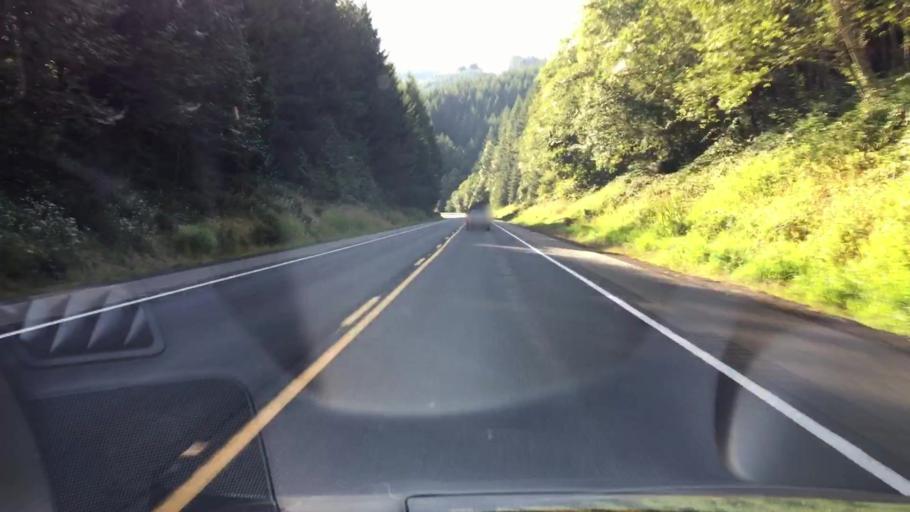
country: US
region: Washington
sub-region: Lewis County
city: Morton
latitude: 46.5417
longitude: -122.3603
